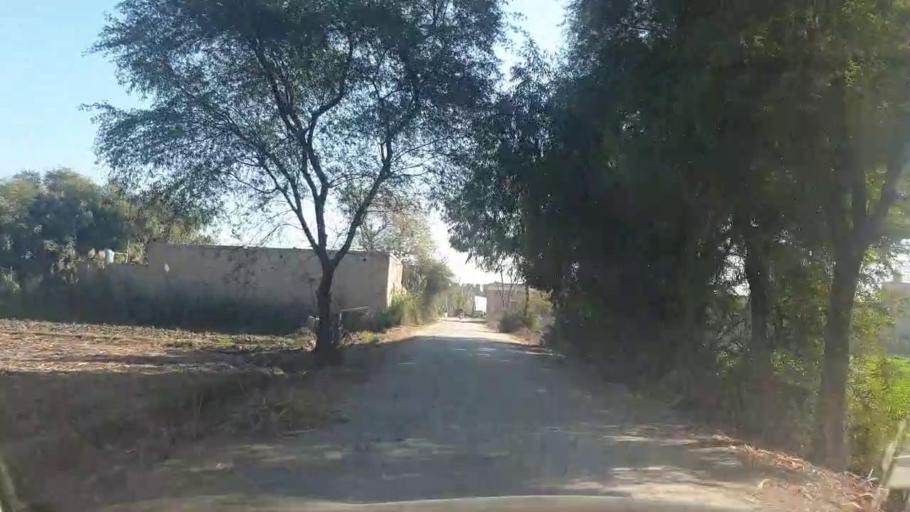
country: PK
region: Sindh
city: Ghotki
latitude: 27.9830
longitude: 69.3180
